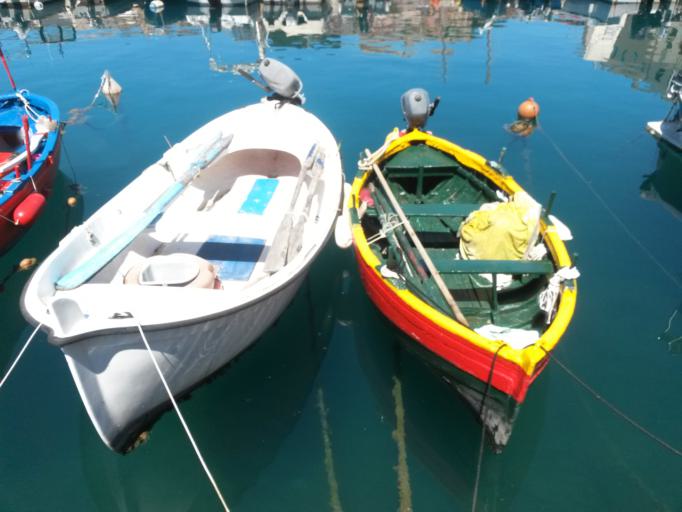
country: IT
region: Tuscany
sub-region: Provincia di Livorno
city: Portoferraio
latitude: 42.8134
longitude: 10.3318
